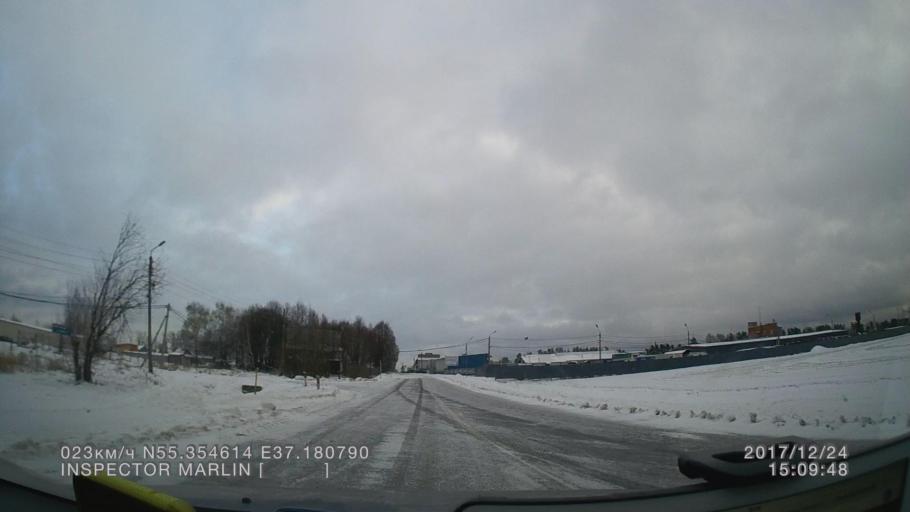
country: RU
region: Moskovskaya
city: Troitsk
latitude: 55.3546
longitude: 37.1808
